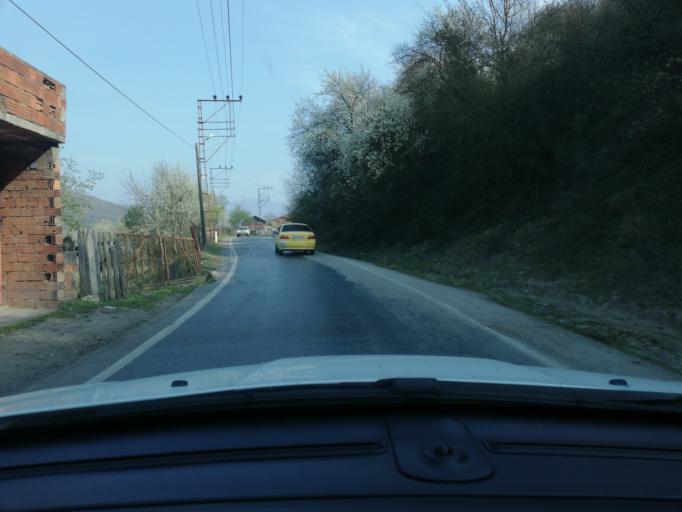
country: TR
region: Karabuk
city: Yenice
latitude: 41.2162
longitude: 32.3634
